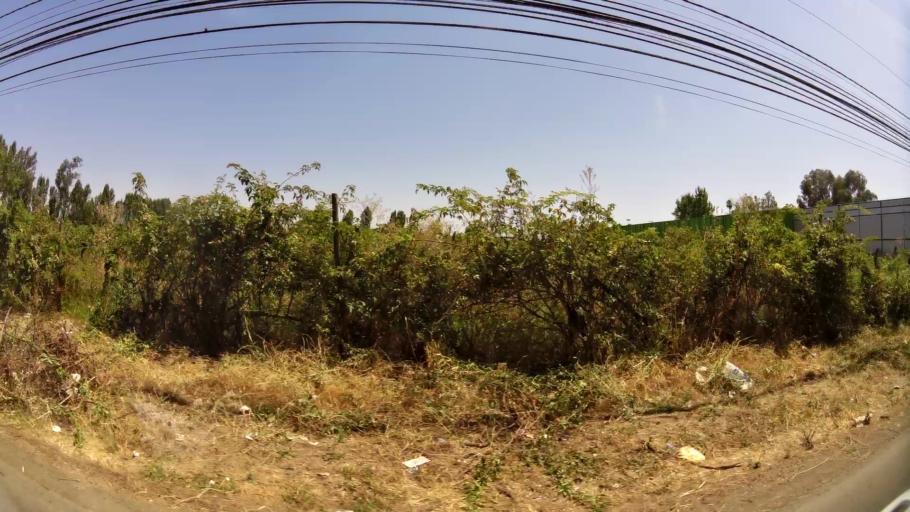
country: CL
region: Maule
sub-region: Provincia de Talca
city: Talca
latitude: -35.4413
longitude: -71.6144
